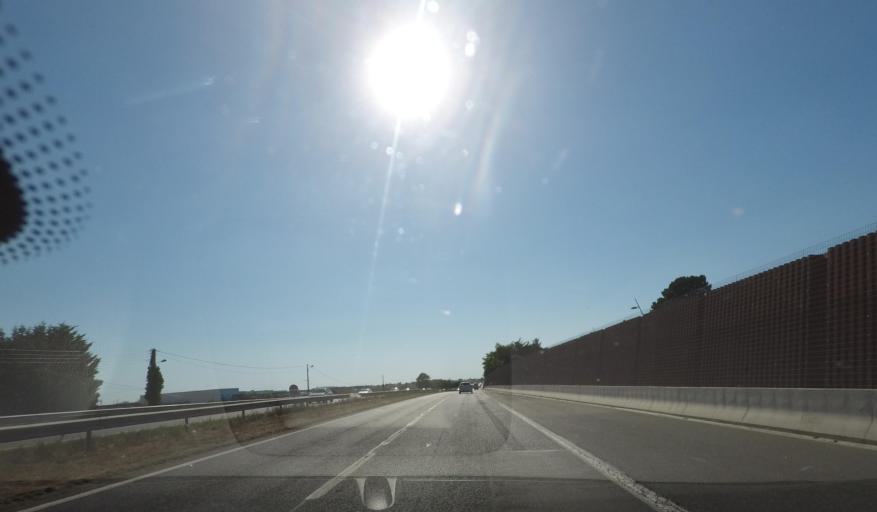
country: FR
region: Pays de la Loire
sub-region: Departement de la Loire-Atlantique
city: Montoir-de-Bretagne
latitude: 47.3261
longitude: -2.1411
